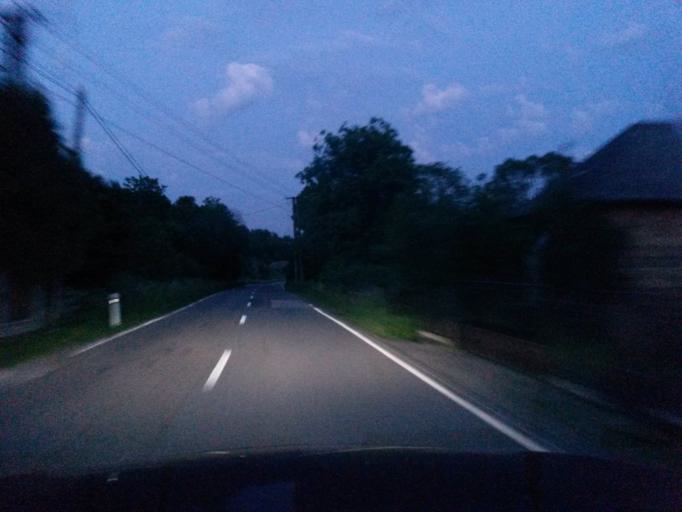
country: UA
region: Zakarpattia
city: Velykyi Bereznyi
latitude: 48.9258
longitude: 22.3123
